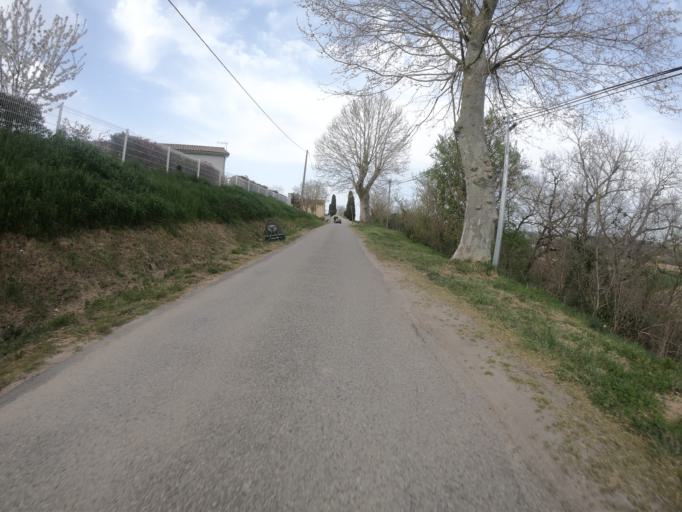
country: FR
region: Languedoc-Roussillon
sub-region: Departement de l'Aude
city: Belpech
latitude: 43.1449
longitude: 1.7136
